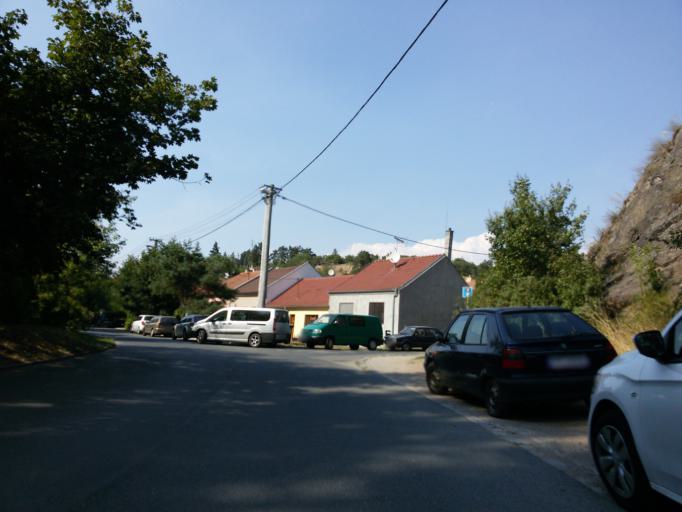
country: CZ
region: South Moravian
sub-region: Mesto Brno
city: Brno
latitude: 49.2285
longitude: 16.5998
